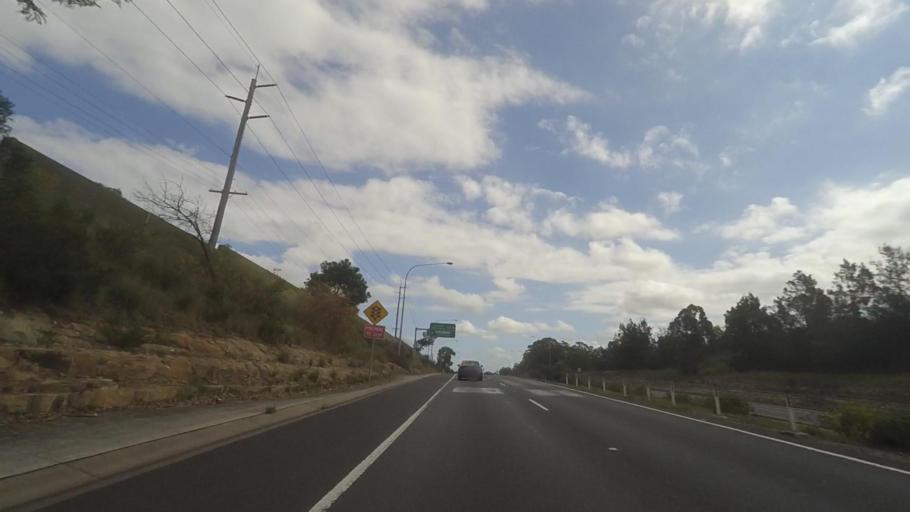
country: AU
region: New South Wales
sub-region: Sutherland Shire
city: Menai
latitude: -34.0211
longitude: 151.0084
